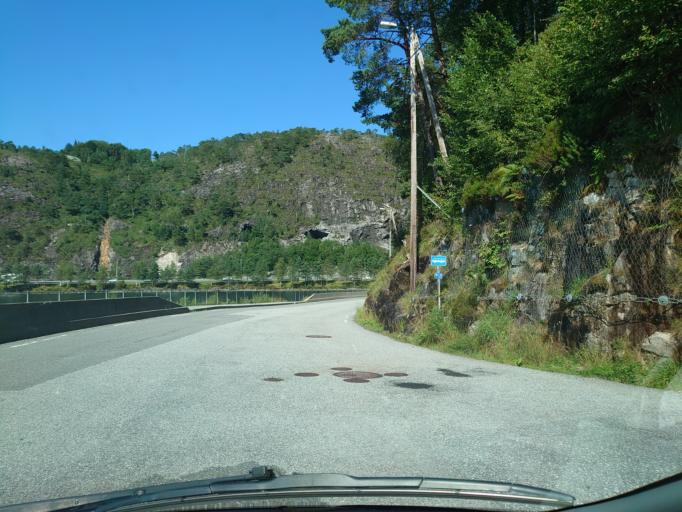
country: NO
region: Hordaland
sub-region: Bergen
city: Ytre Arna
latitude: 60.4580
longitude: 5.4190
